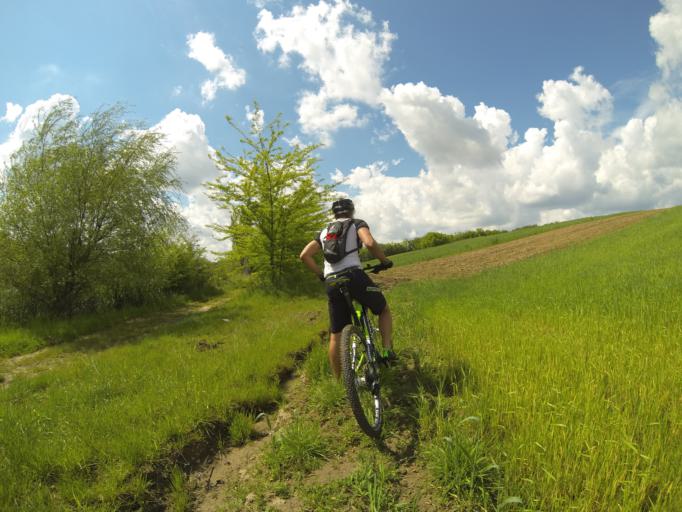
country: RO
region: Dolj
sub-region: Comuna Malu Mare
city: Preajba
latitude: 44.2661
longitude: 23.8559
